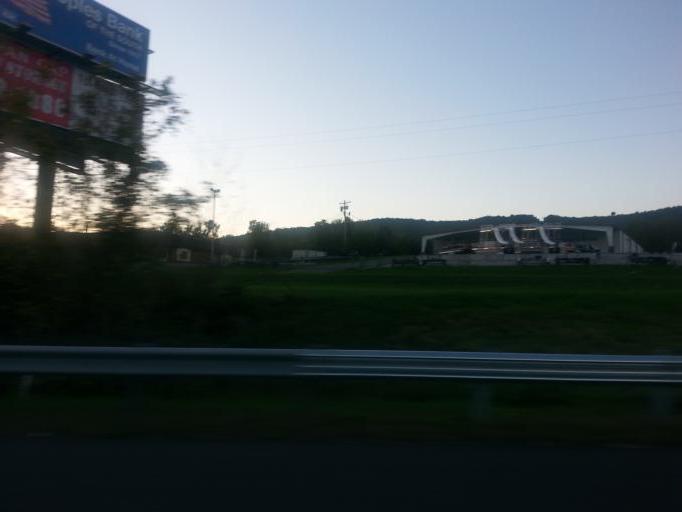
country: US
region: Tennessee
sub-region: Campbell County
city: Jacksboro
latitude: 36.3283
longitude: -84.1927
